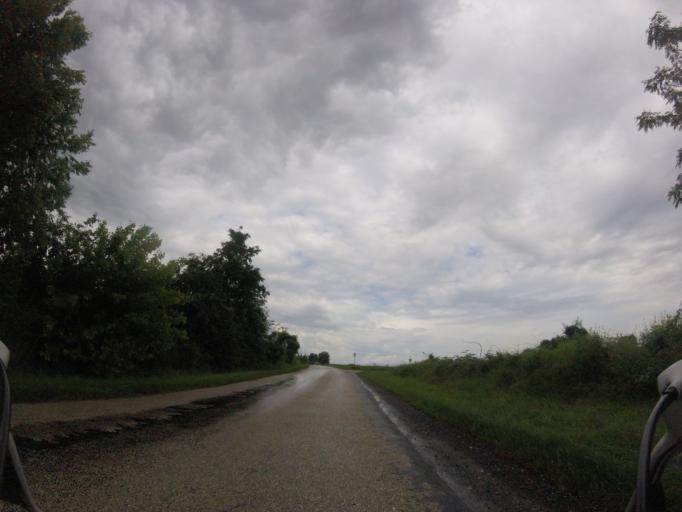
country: HU
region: Baranya
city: Pellerd
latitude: 45.9539
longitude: 18.2186
